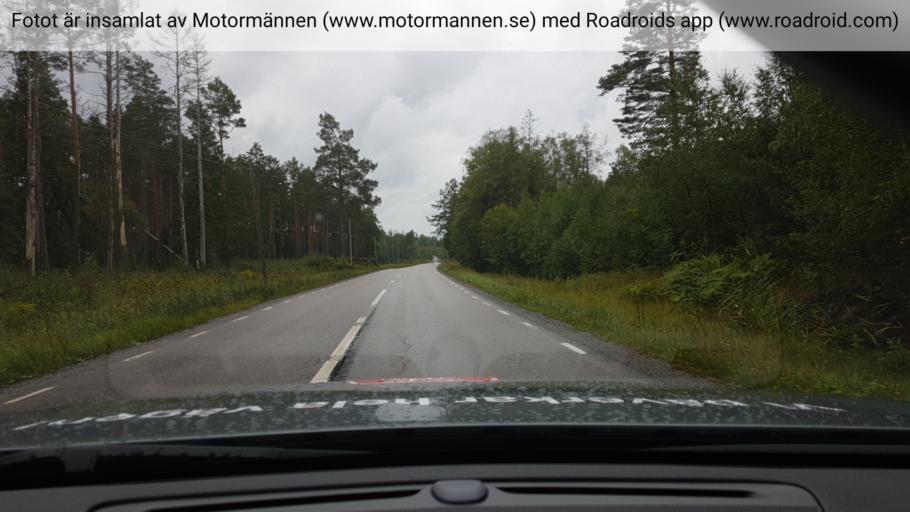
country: SE
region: Stockholm
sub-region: Botkyrka Kommun
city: Tullinge
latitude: 59.1887
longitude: 17.9291
